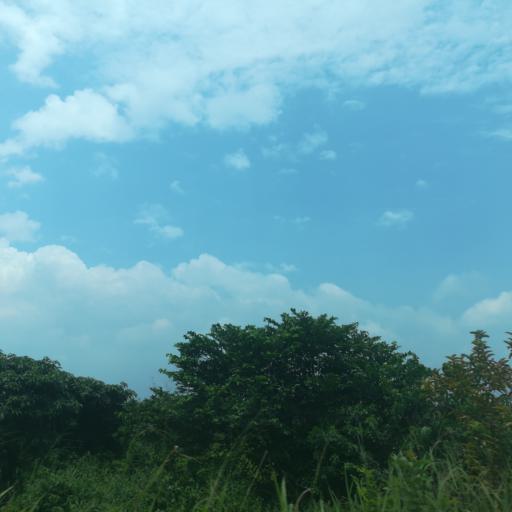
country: NG
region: Lagos
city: Ejirin
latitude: 6.6575
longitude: 3.8035
